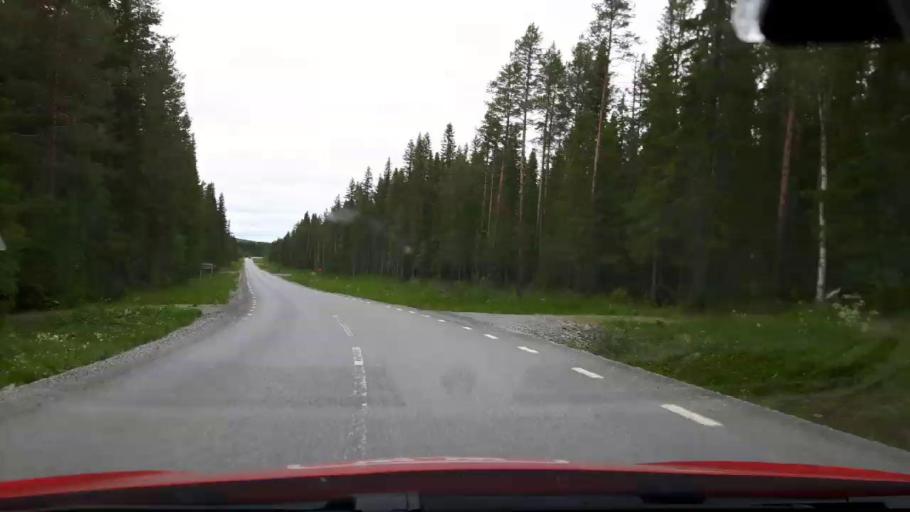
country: SE
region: Jaemtland
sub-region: OEstersunds Kommun
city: Lit
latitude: 63.6767
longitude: 14.6883
